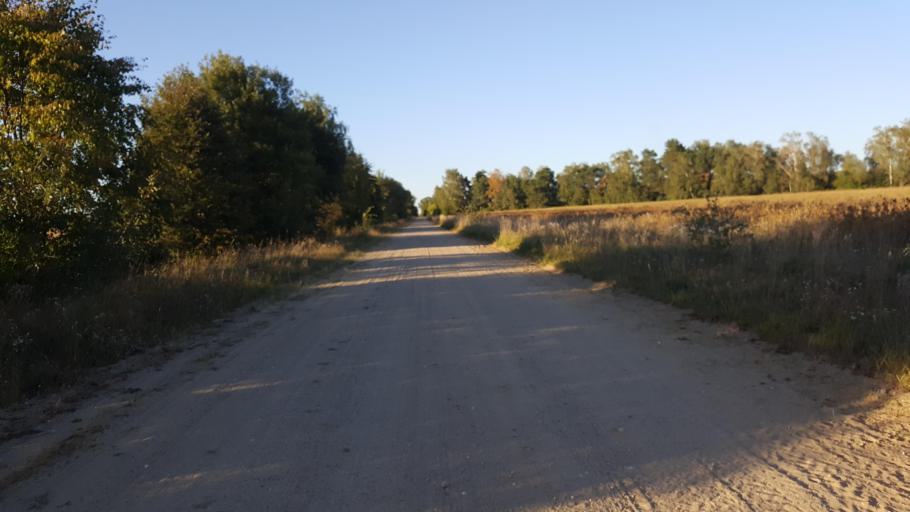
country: BY
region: Brest
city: Vysokaye
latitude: 52.3234
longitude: 23.4336
